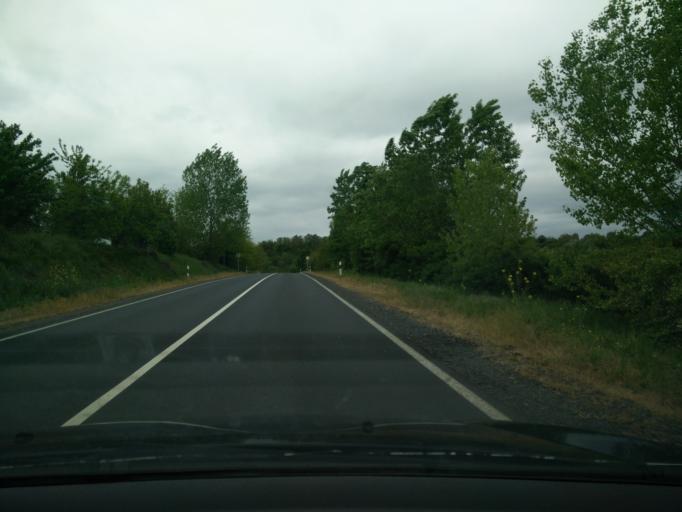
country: HU
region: Zala
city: Turje
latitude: 46.9816
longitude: 17.1210
